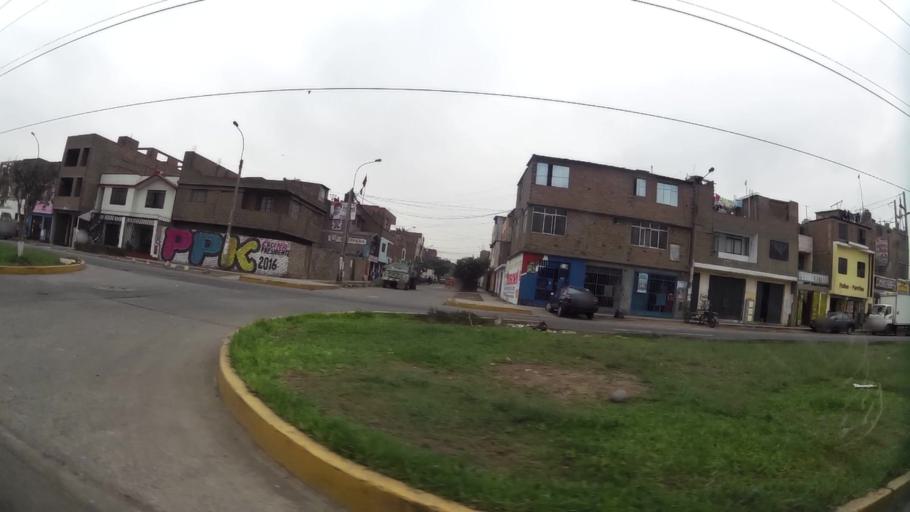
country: PE
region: Lima
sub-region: Lima
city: Vitarte
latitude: -12.0401
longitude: -76.9716
